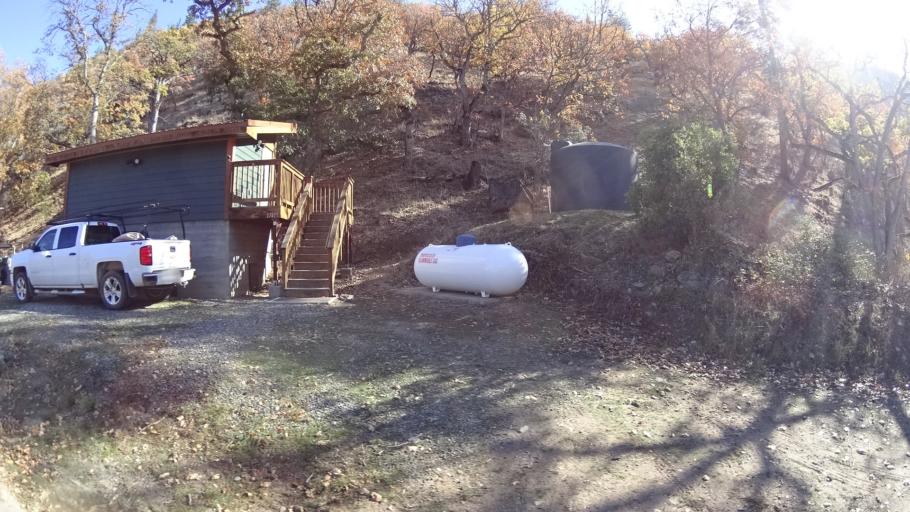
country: US
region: California
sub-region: Siskiyou County
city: Yreka
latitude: 41.8643
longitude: -122.8178
